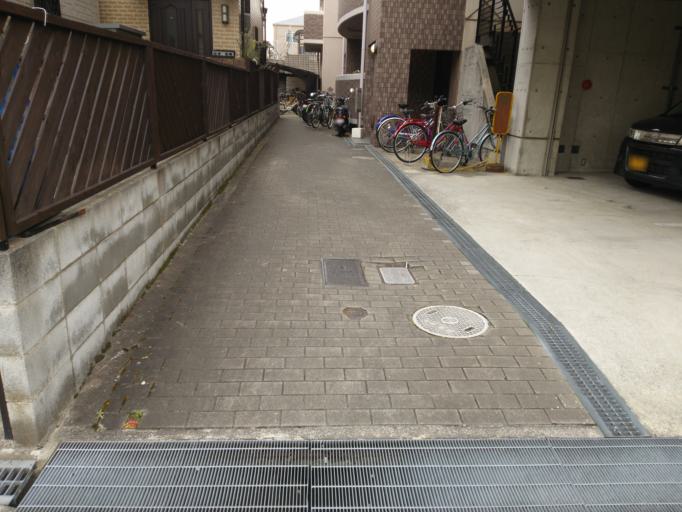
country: JP
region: Hyogo
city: Amagasaki
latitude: 34.7274
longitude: 135.4127
